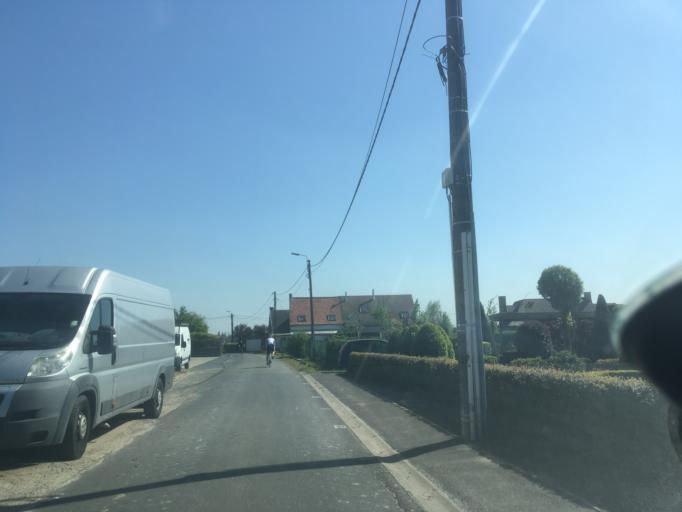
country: BE
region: Flanders
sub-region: Provincie West-Vlaanderen
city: Ardooie
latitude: 50.9525
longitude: 3.2258
